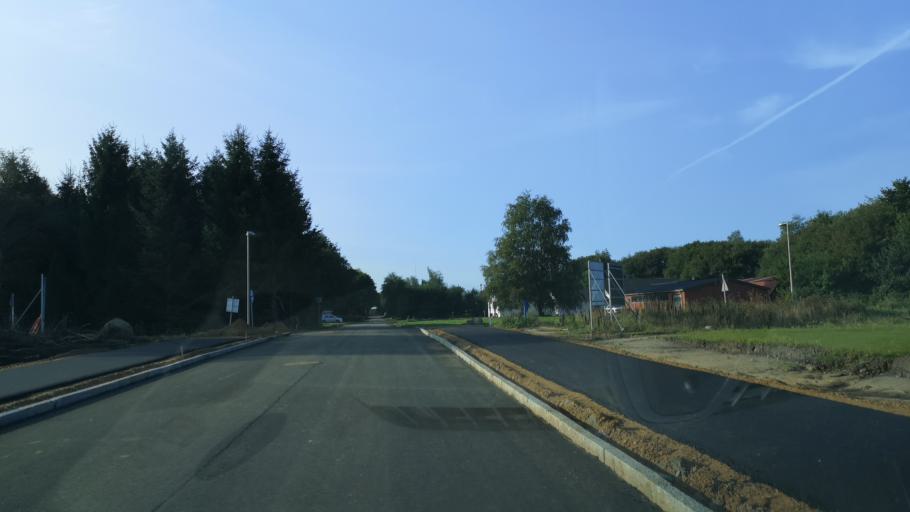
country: DK
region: Central Jutland
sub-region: Herning Kommune
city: Snejbjerg
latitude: 56.1389
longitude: 8.9191
